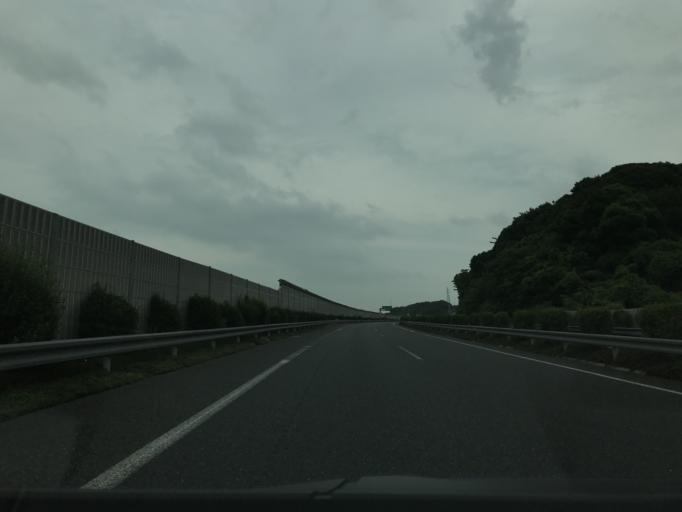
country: JP
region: Fukuoka
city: Kanda
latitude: 33.7981
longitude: 130.9614
